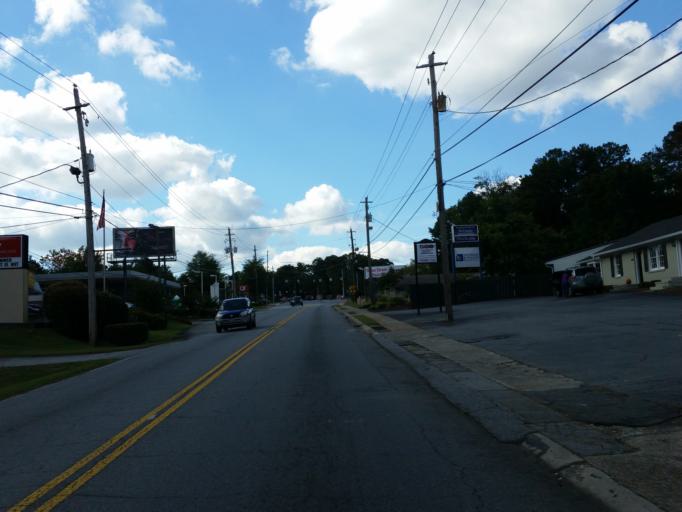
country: US
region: Georgia
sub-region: Cobb County
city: Marietta
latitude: 33.9506
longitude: -84.4948
